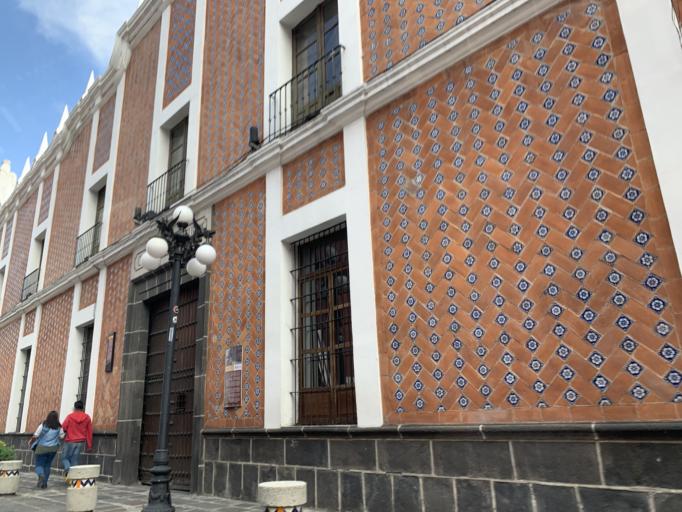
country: MX
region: Puebla
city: Puebla
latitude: 19.0425
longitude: -98.1987
